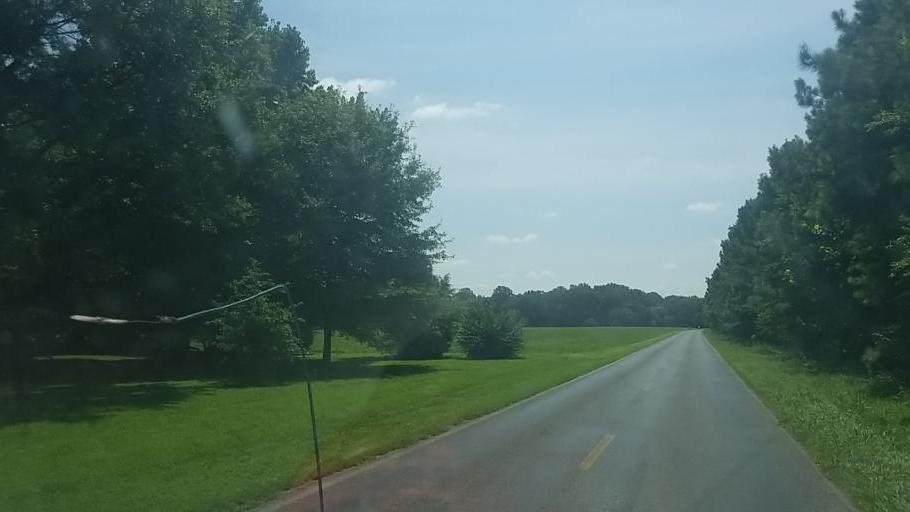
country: US
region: Maryland
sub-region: Caroline County
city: Ridgely
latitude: 38.8887
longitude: -75.9275
